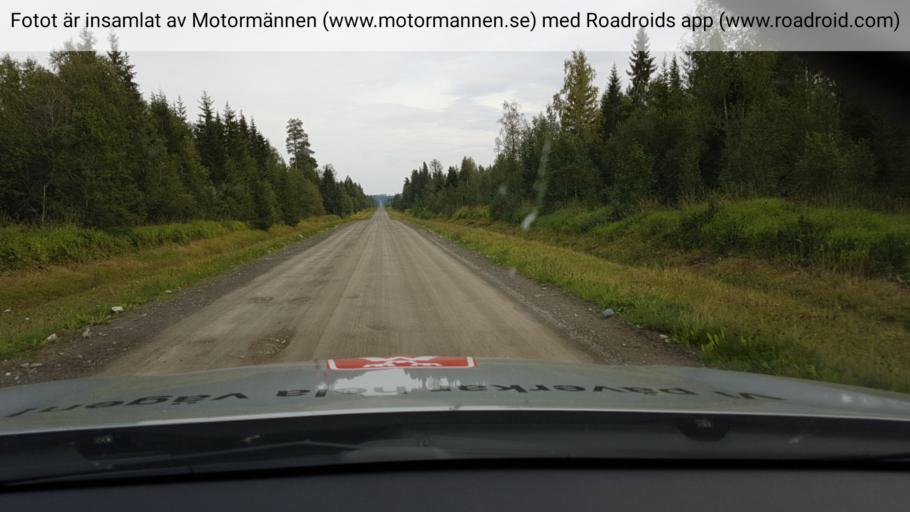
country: SE
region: Jaemtland
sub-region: OEstersunds Kommun
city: Lit
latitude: 63.6750
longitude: 14.8744
